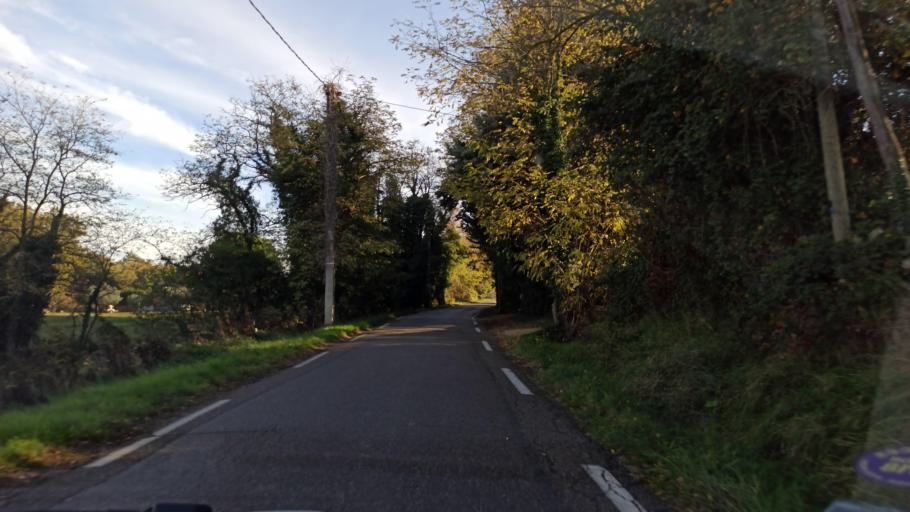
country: FR
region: Provence-Alpes-Cote d'Azur
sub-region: Departement du Vaucluse
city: Goult
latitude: 43.8468
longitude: 5.2459
